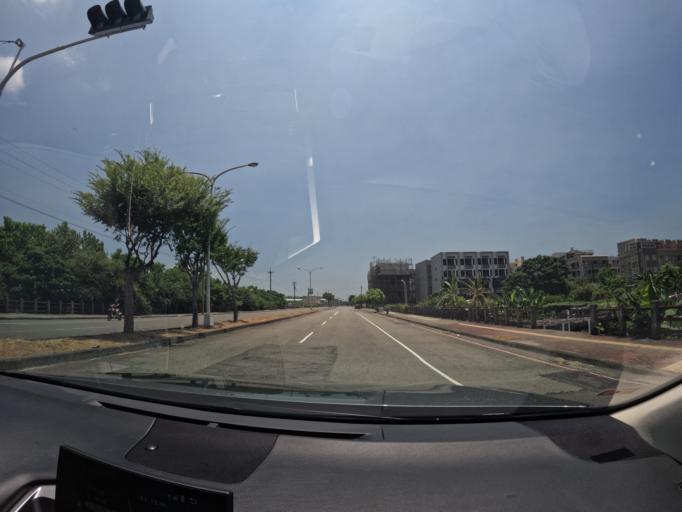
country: TW
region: Taiwan
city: Fengyuan
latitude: 24.2527
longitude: 120.5606
